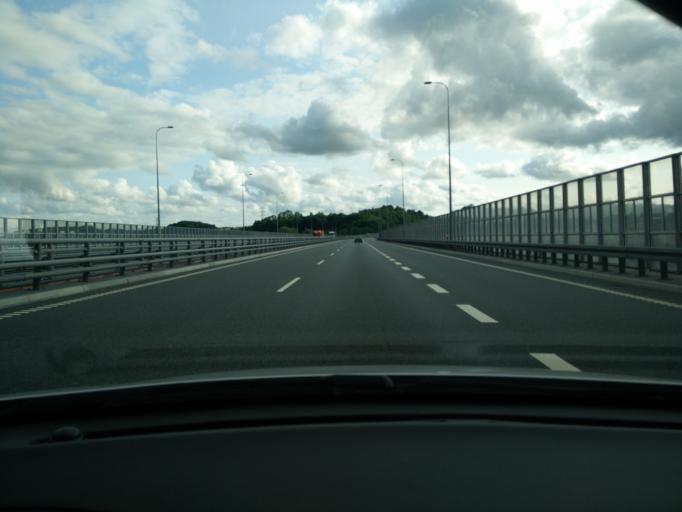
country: PL
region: Pomeranian Voivodeship
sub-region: Powiat gdanski
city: Pruszcz Gdanski
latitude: 54.3021
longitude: 18.6397
